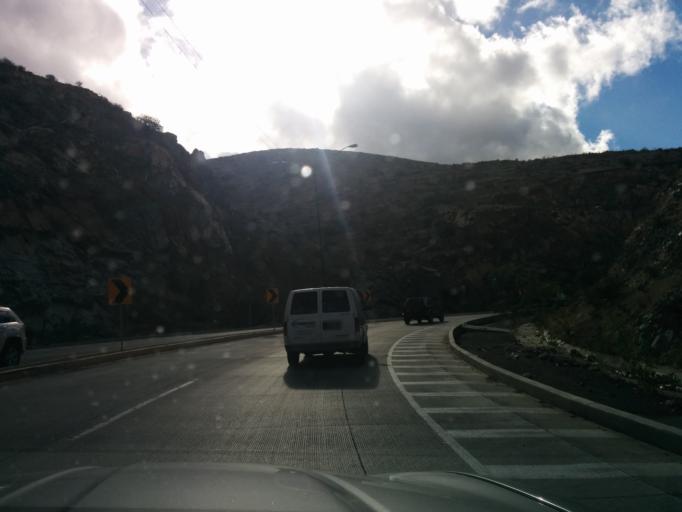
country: MX
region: Baja California
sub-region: Tijuana
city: Ejido Javier Rojo Gomez
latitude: 32.5421
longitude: -116.8526
